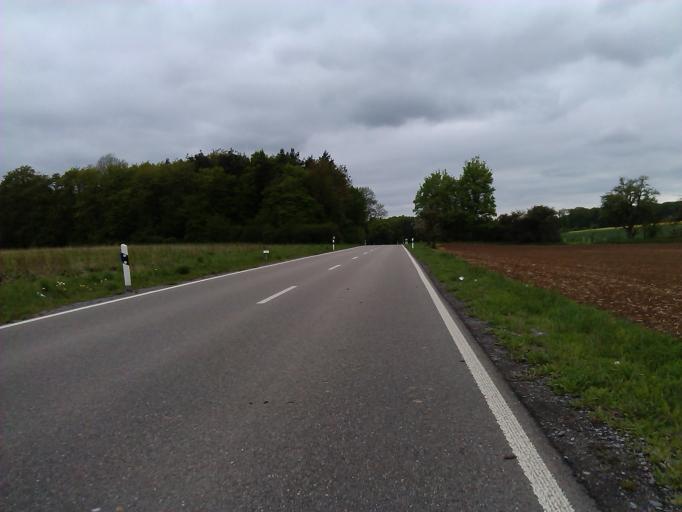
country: DE
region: Baden-Wuerttemberg
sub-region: Karlsruhe Region
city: Sternenfels
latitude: 49.0566
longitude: 8.8765
